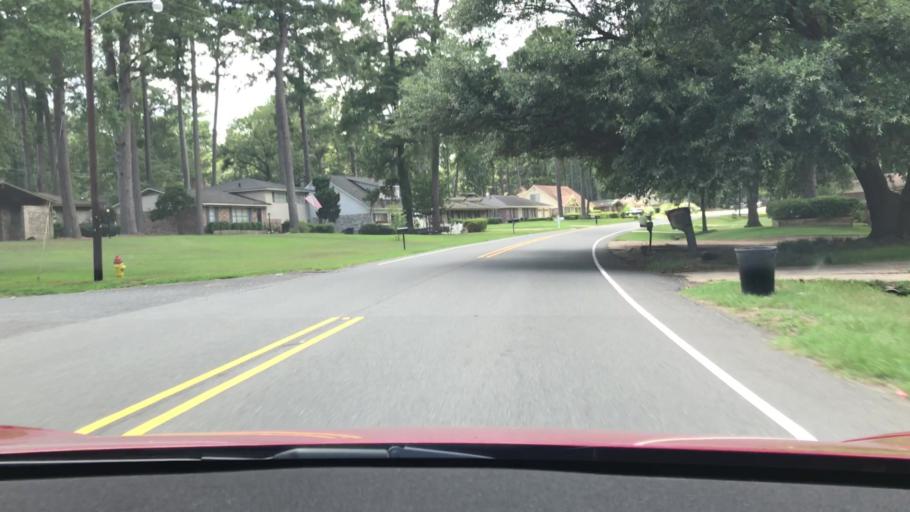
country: US
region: Louisiana
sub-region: De Soto Parish
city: Stonewall
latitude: 32.3892
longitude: -93.7922
